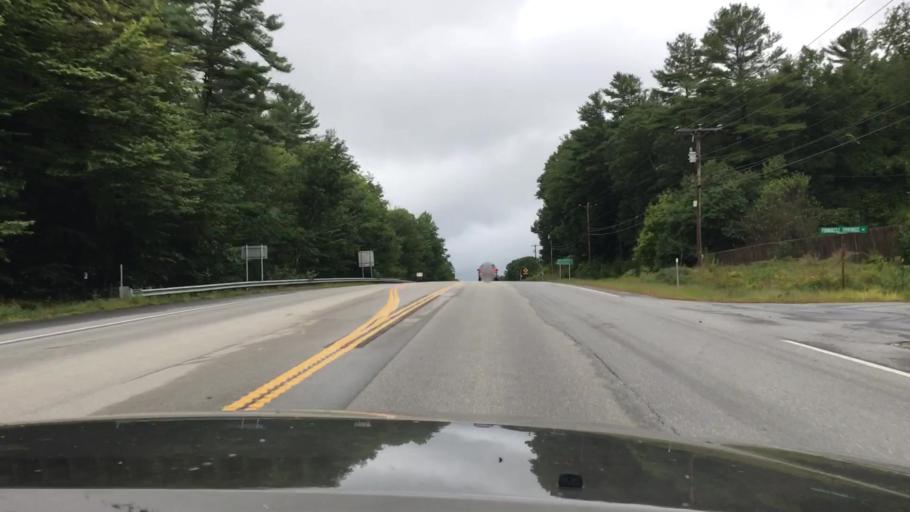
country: US
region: New Hampshire
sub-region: Cheshire County
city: Chesterfield
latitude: 42.9014
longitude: -72.4613
